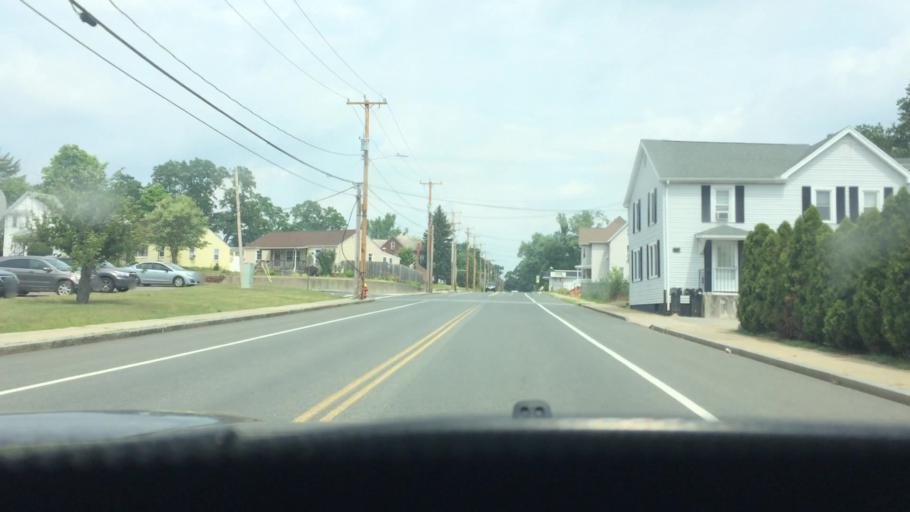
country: US
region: Massachusetts
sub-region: Hampden County
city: North Chicopee
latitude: 42.1634
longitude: -72.5829
